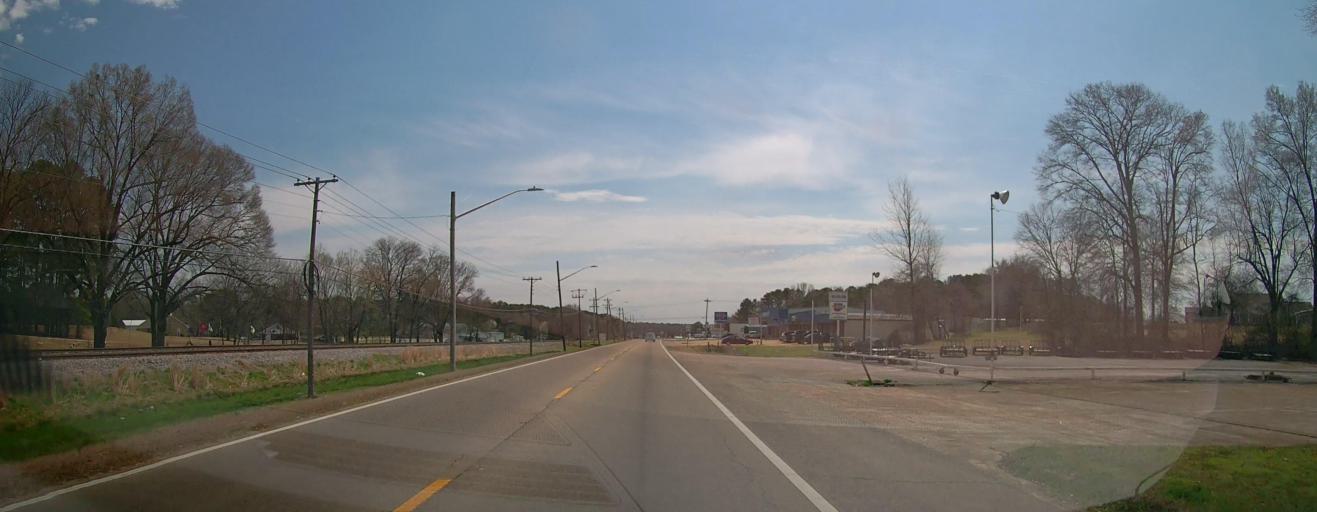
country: US
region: Mississippi
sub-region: Union County
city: New Albany
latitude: 34.5056
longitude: -89.0302
